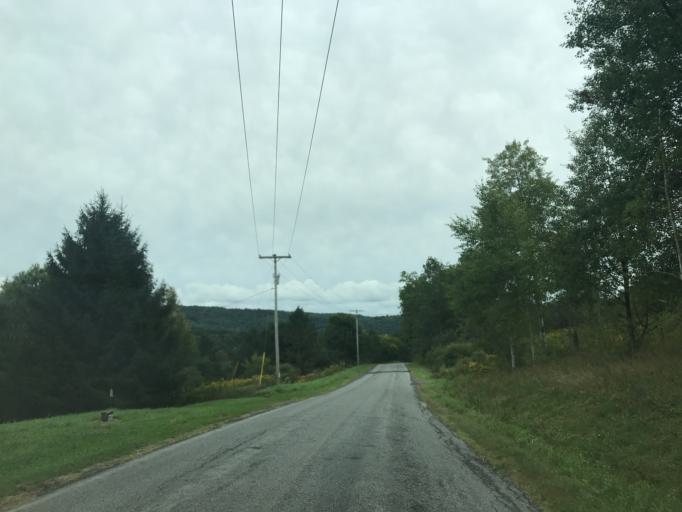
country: US
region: New York
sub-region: Otsego County
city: Worcester
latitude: 42.5566
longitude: -74.6654
